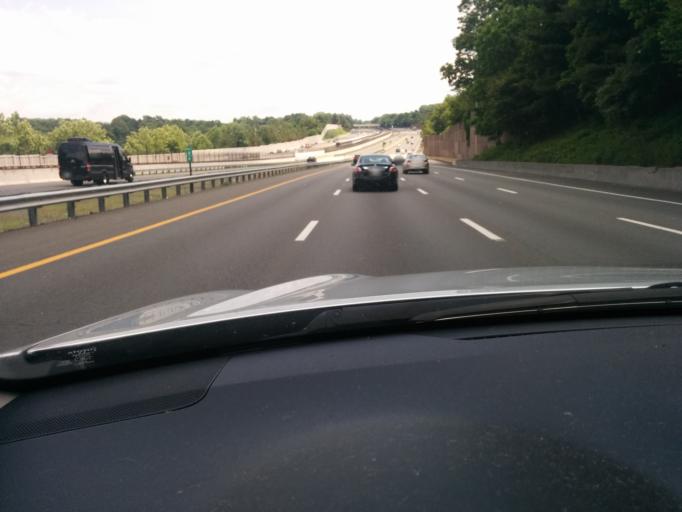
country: US
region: Virginia
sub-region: Fairfax County
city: Wolf Trap
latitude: 38.9462
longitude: -77.2955
